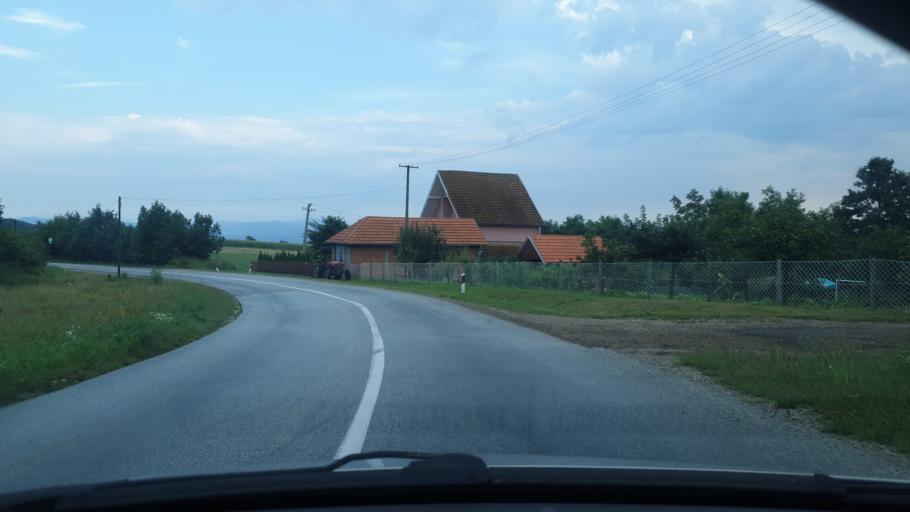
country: RS
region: Central Serbia
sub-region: Sumadijski Okrug
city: Kragujevac
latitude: 44.0464
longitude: 20.7867
